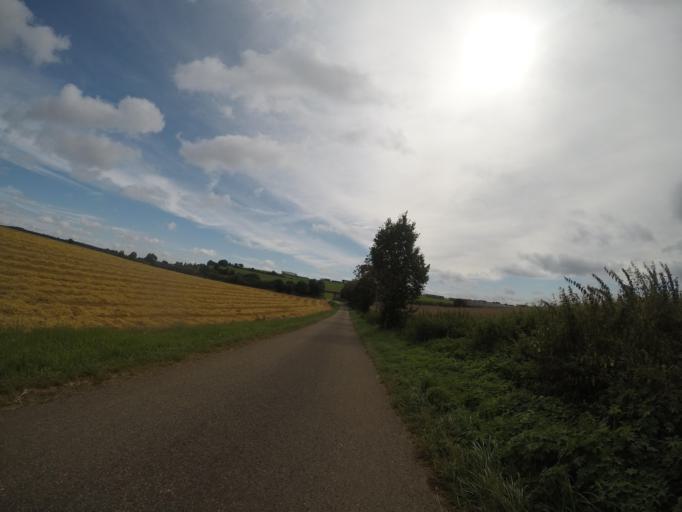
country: DE
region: Baden-Wuerttemberg
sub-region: Tuebingen Region
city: Laichingen
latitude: 48.4554
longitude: 9.6603
